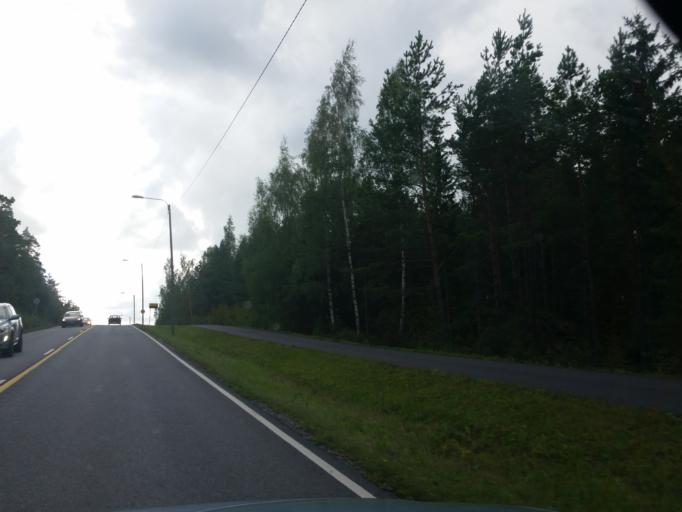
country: FI
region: Varsinais-Suomi
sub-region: Aboland-Turunmaa
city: Laensi-Turunmaa
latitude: 60.2913
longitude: 22.2644
